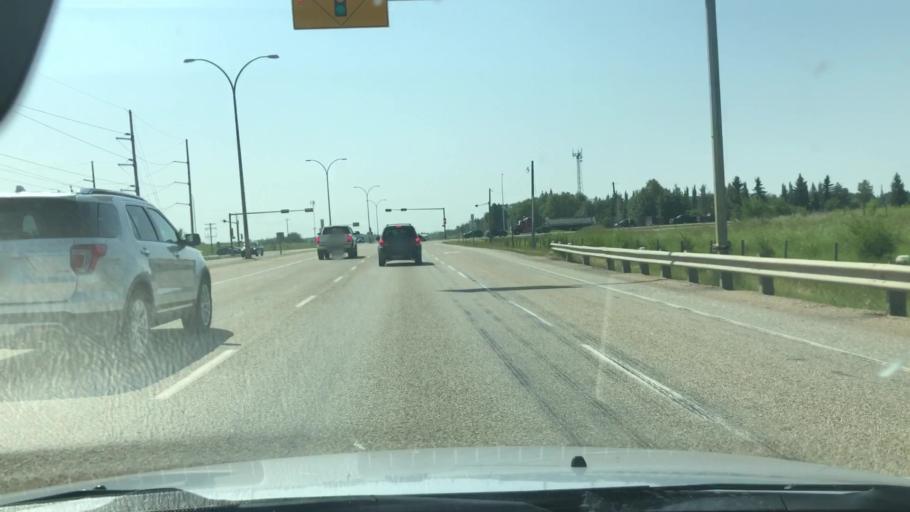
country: CA
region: Alberta
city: Devon
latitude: 53.4555
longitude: -113.7626
